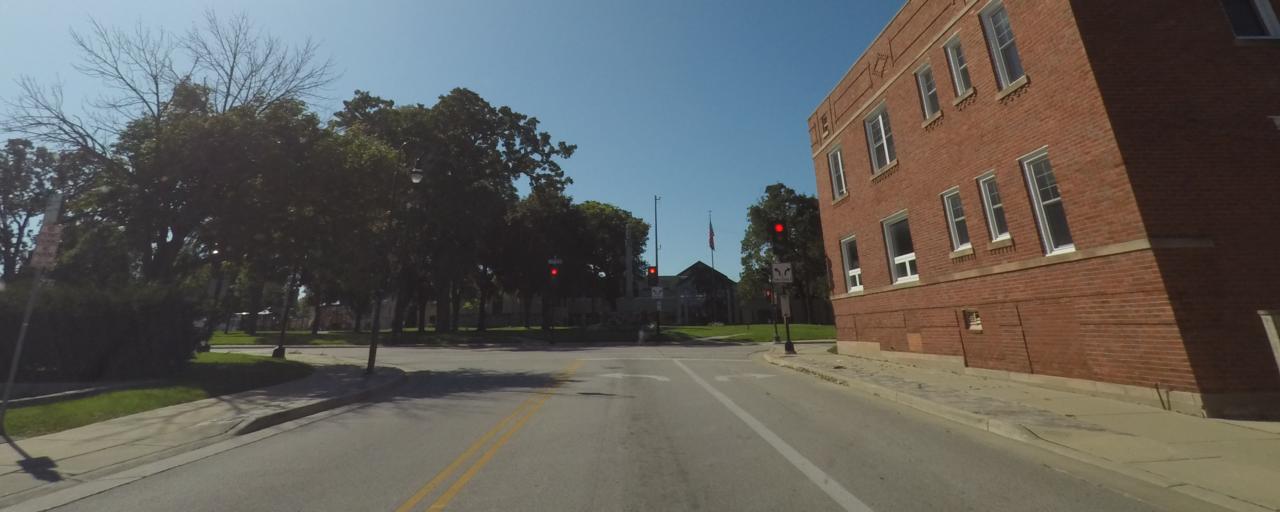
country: US
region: Wisconsin
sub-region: Waukesha County
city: Waukesha
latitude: 43.0101
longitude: -88.2327
